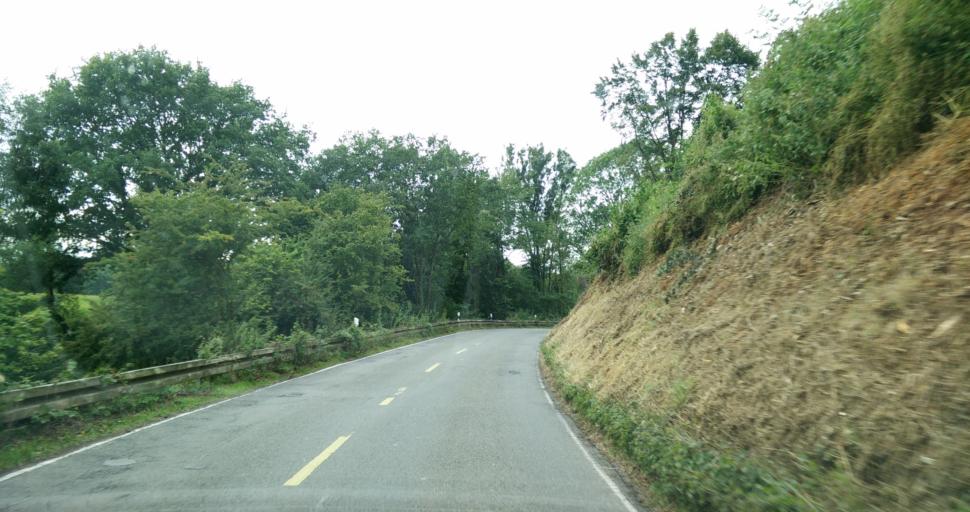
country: DE
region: North Rhine-Westphalia
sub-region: Regierungsbezirk Dusseldorf
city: Ratingen
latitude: 51.2795
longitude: 6.8867
